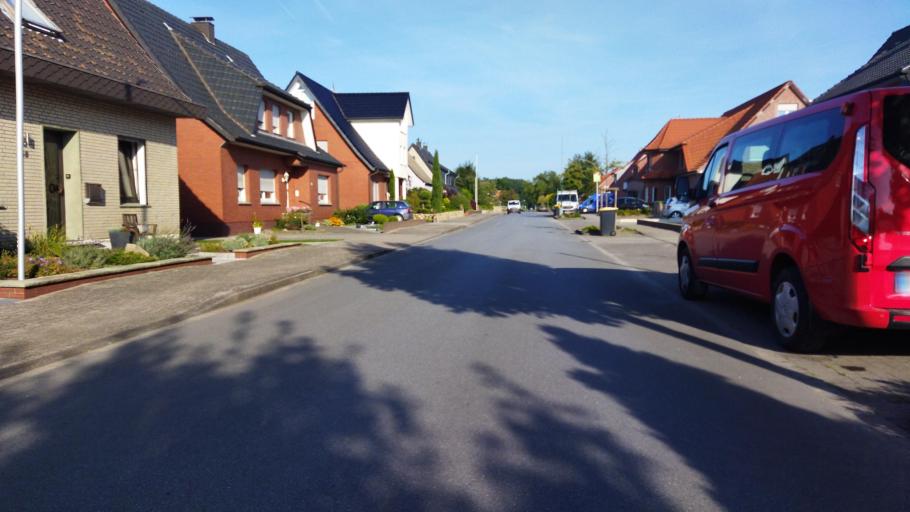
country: DE
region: Lower Saxony
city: Bad Laer
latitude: 52.0995
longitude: 8.0578
